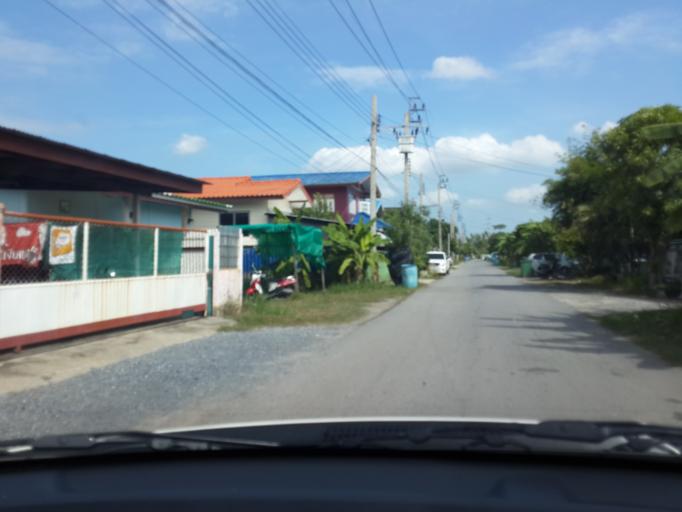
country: TH
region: Bangkok
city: Khlong Sam Wa
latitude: 13.8464
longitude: 100.7838
